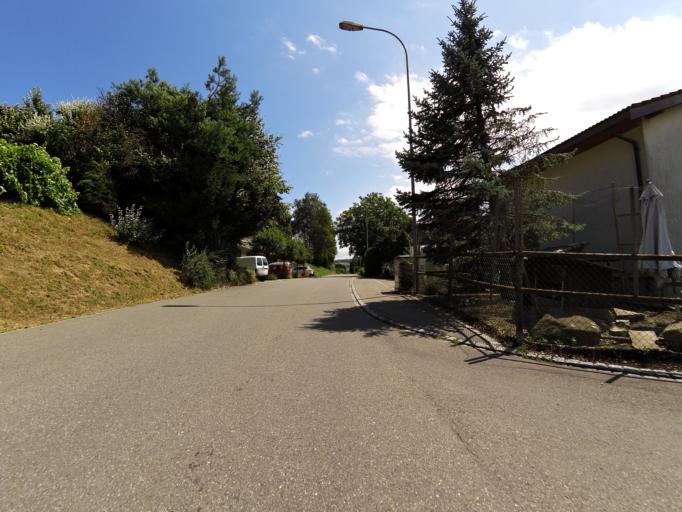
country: CH
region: Thurgau
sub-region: Weinfelden District
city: Wigoltingen
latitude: 47.5977
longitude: 9.0330
